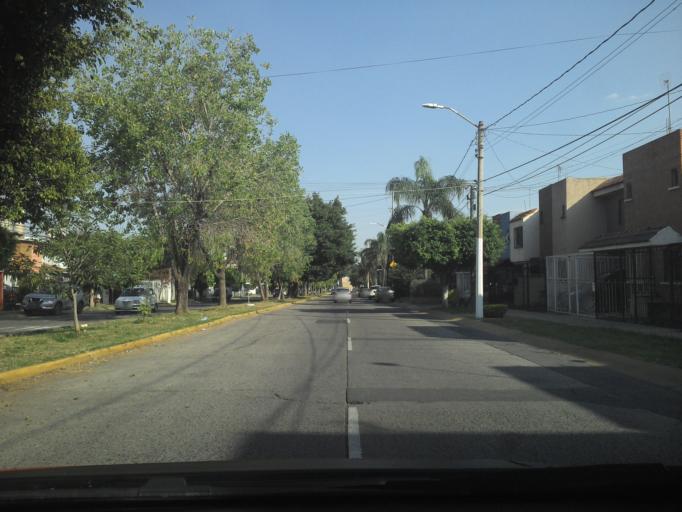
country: MX
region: Jalisco
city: Guadalajara
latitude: 20.6527
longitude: -103.4432
